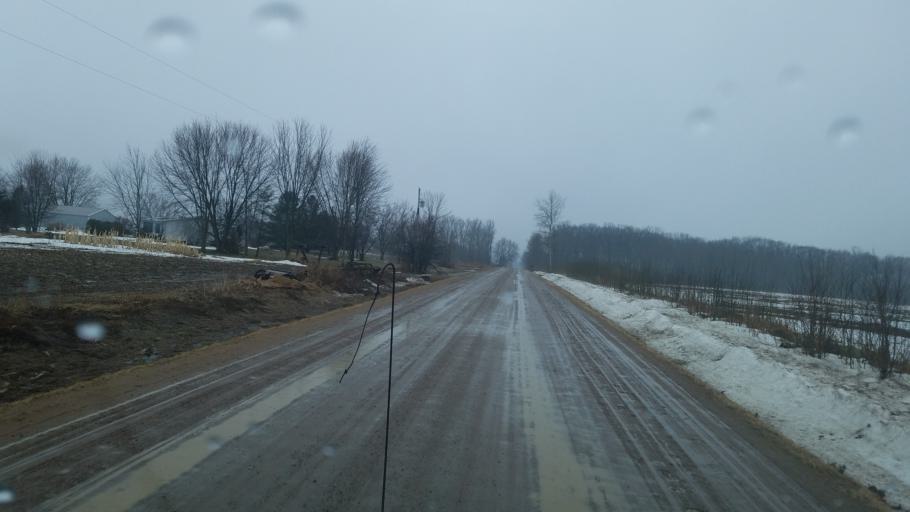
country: US
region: Wisconsin
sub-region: Clark County
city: Loyal
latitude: 44.6383
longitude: -90.3973
